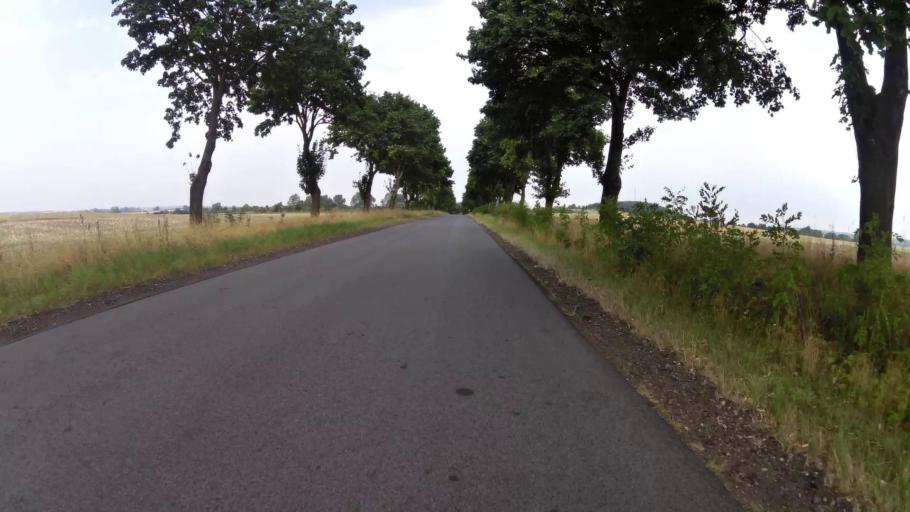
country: PL
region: West Pomeranian Voivodeship
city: Trzcinsko Zdroj
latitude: 52.9518
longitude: 14.6304
